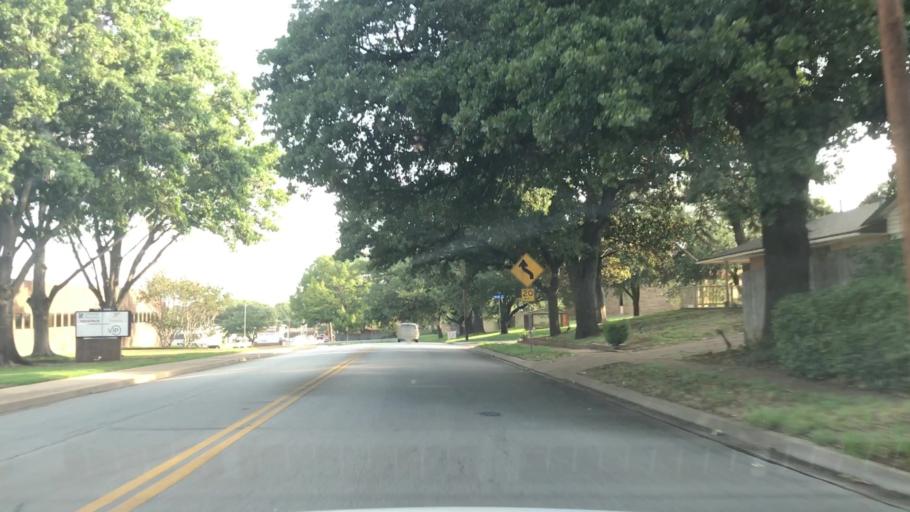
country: US
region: Texas
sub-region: Tarrant County
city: Arlington
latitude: 32.7474
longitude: -97.1229
